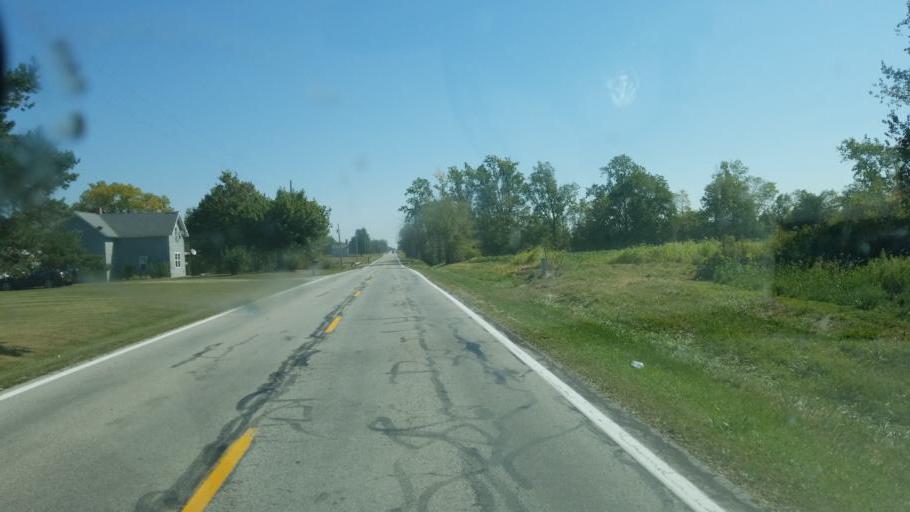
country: US
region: Ohio
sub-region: Wyandot County
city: Upper Sandusky
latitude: 40.6436
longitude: -83.3600
